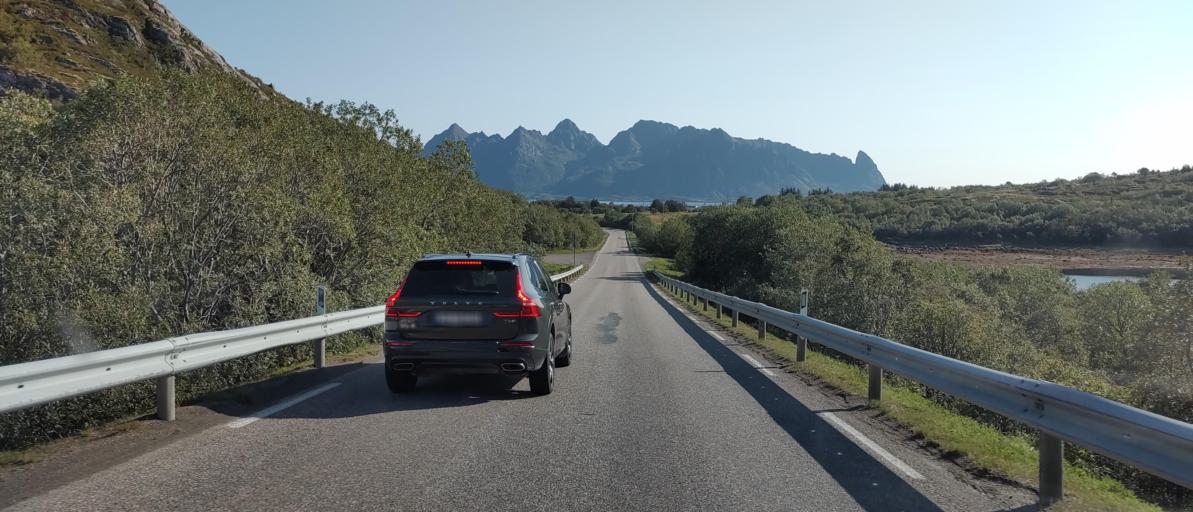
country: NO
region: Nordland
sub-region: Vagan
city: Svolvaer
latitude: 68.2445
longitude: 14.6417
